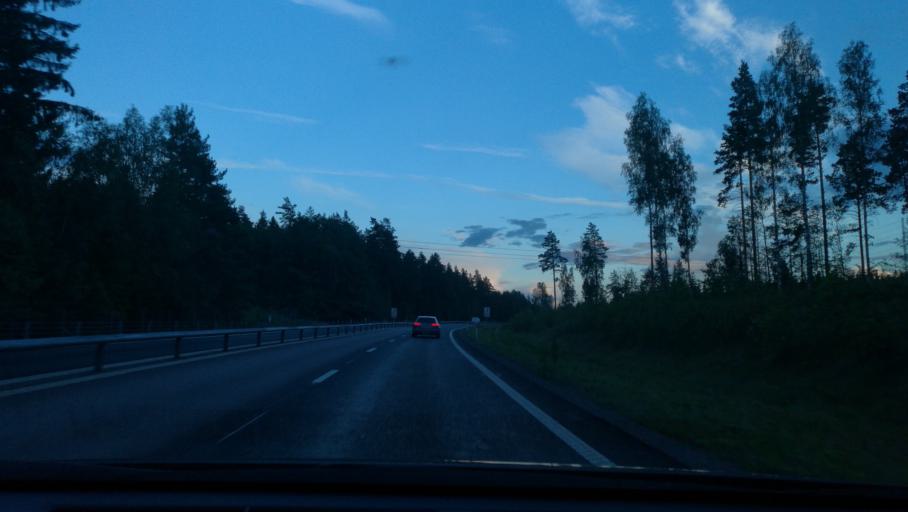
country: SE
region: Soedermanland
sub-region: Katrineholms Kommun
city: Katrineholm
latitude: 58.9009
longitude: 16.2066
